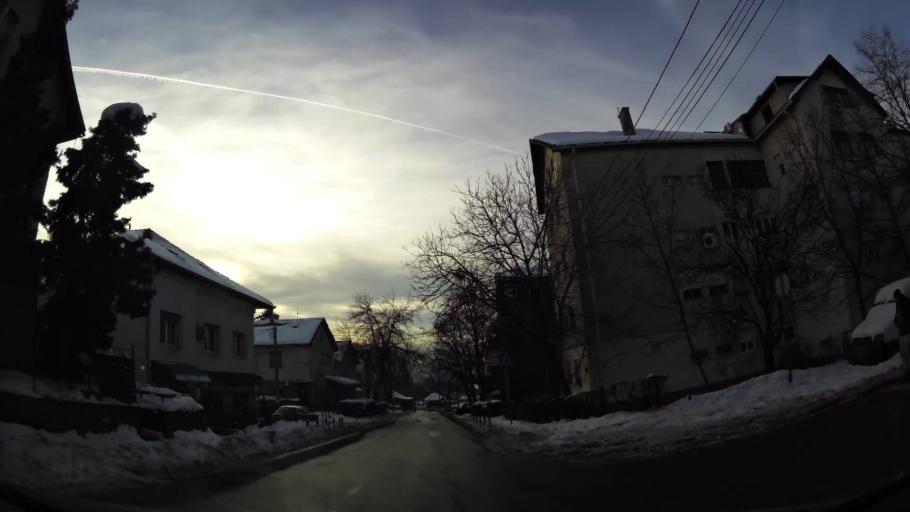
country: RS
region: Central Serbia
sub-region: Belgrade
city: Palilula
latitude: 44.8087
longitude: 20.4954
